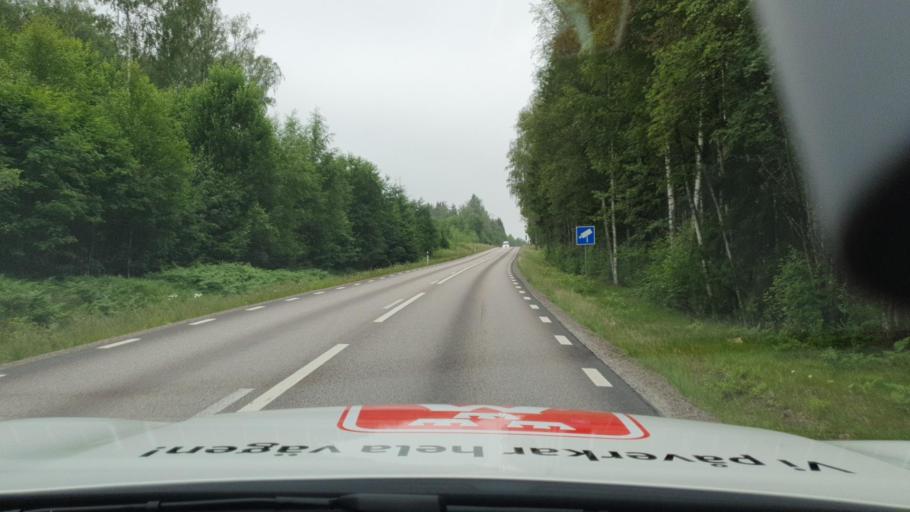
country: SE
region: Vaermland
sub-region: Karlstads Kommun
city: Edsvalla
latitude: 59.6060
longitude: 13.1569
